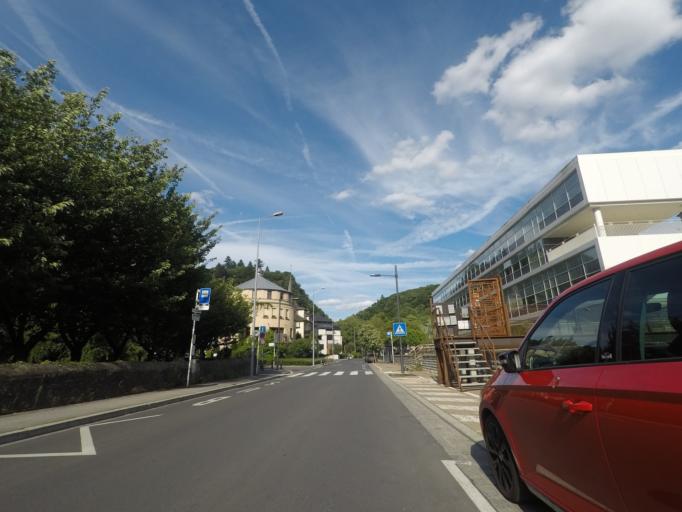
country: LU
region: Luxembourg
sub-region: Canton de Luxembourg
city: Luxembourg
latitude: 49.6143
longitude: 6.1410
